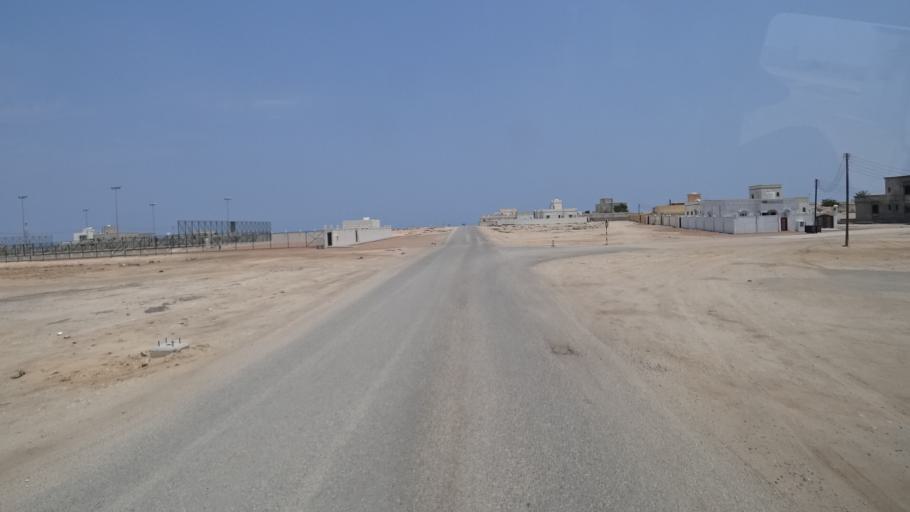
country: OM
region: Ash Sharqiyah
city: Sur
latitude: 22.5269
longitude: 59.7933
